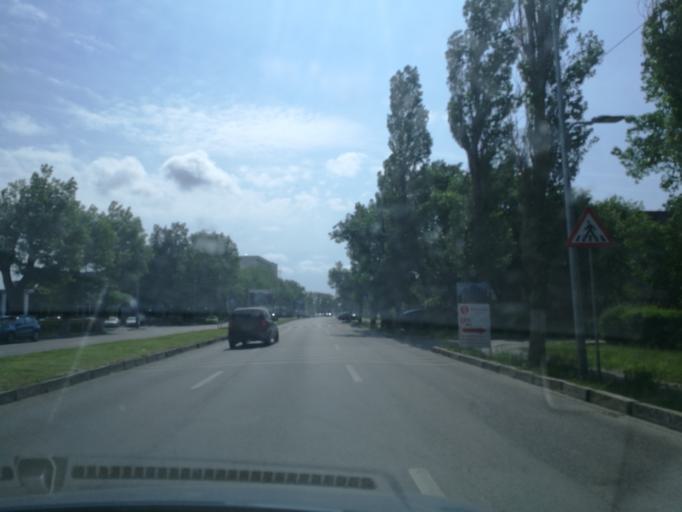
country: RO
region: Constanta
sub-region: Municipiul Constanta
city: Palazu Mare
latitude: 44.2179
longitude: 28.6358
